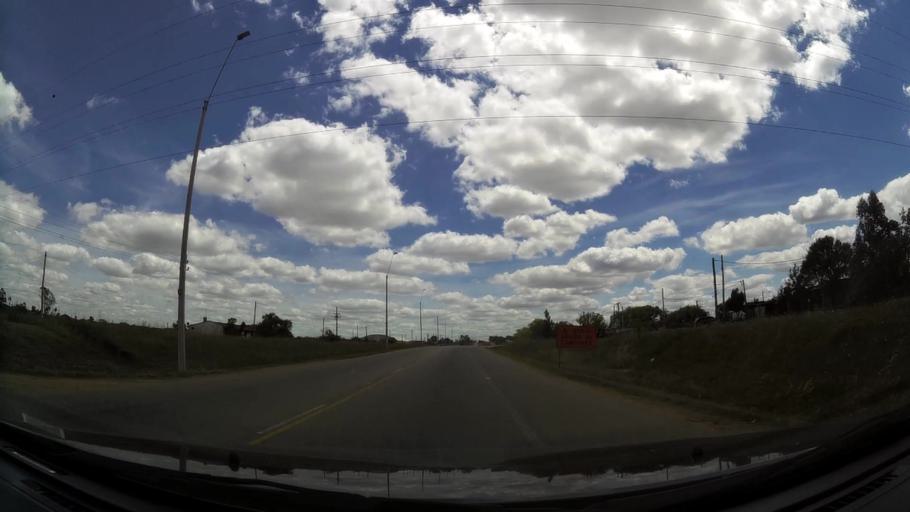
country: UY
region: Canelones
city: Colonia Nicolich
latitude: -34.7964
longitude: -56.0033
